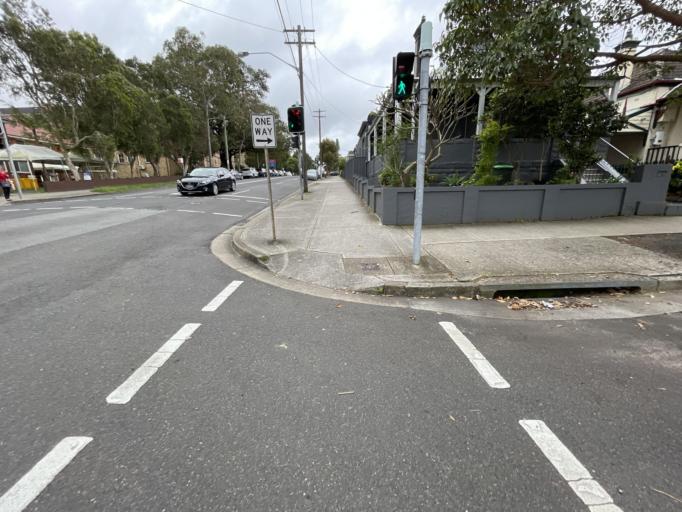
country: AU
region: New South Wales
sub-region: Randwick
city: Randwick
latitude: -33.9199
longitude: 151.2407
